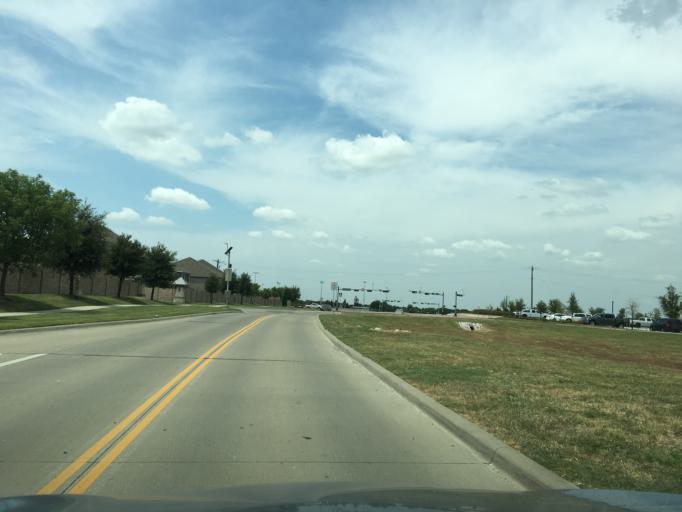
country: US
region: Texas
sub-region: Denton County
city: The Colony
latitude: 33.0350
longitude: -96.9222
